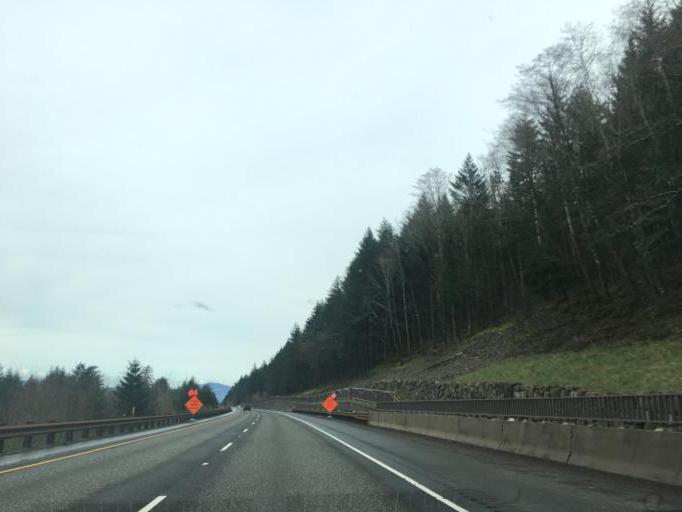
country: US
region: Oregon
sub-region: Hood River County
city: Cascade Locks
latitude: 45.6208
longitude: -121.9827
